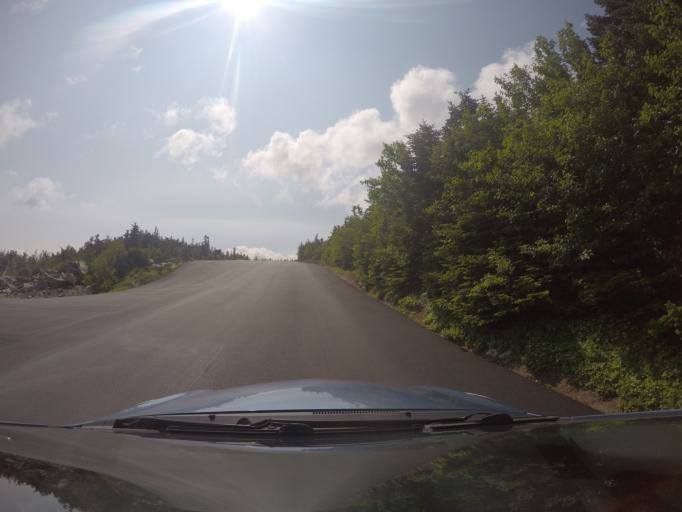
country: US
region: New Hampshire
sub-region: Coos County
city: Gorham
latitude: 44.2922
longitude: -71.2810
